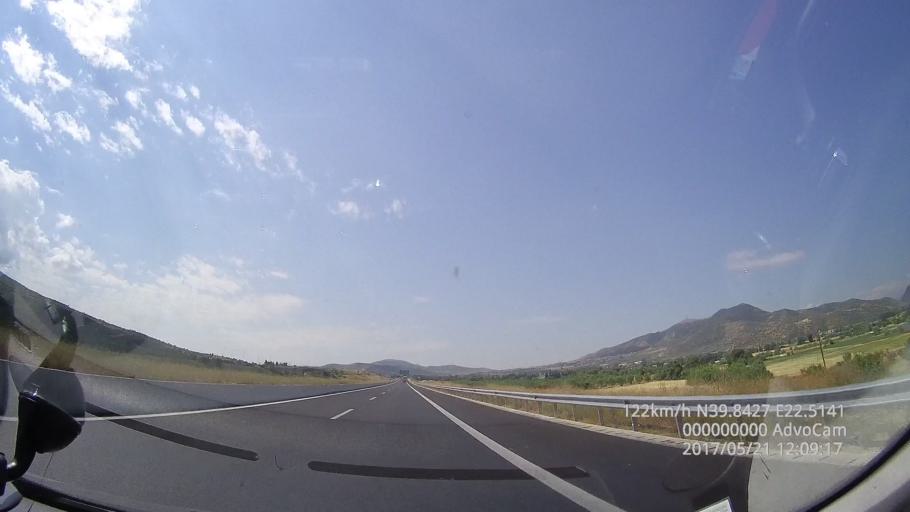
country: GR
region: Thessaly
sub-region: Nomos Larisis
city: Gonnoi
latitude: 39.8419
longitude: 22.5140
